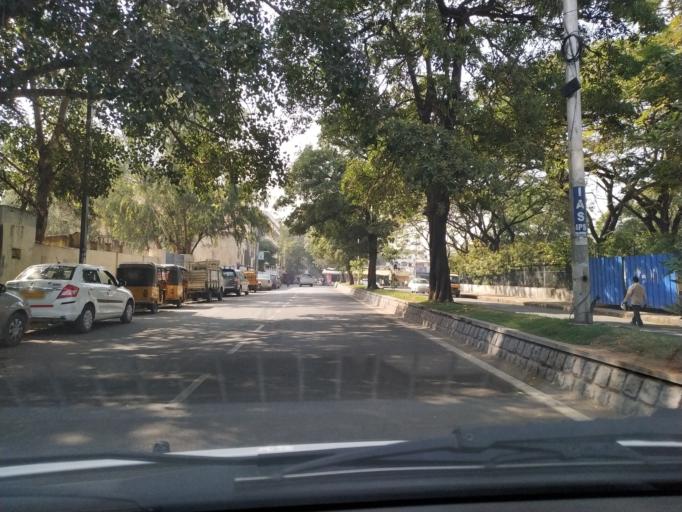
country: IN
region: Telangana
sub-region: Hyderabad
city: Hyderabad
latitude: 17.4105
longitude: 78.4659
